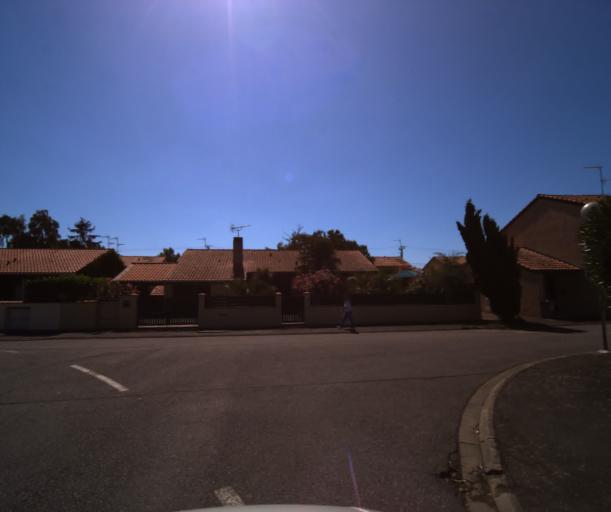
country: FR
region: Midi-Pyrenees
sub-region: Departement de la Haute-Garonne
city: Muret
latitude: 43.4690
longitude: 1.3257
